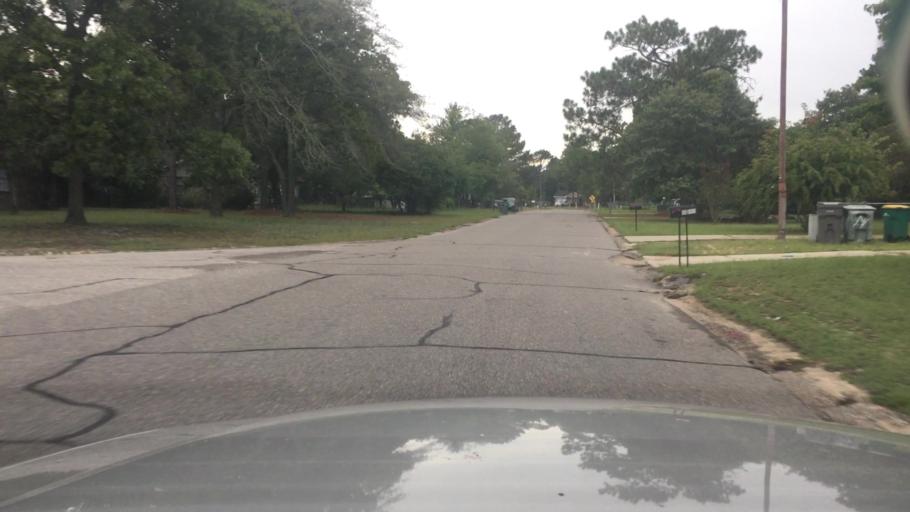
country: US
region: North Carolina
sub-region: Cumberland County
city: Hope Mills
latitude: 34.9727
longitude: -78.9724
